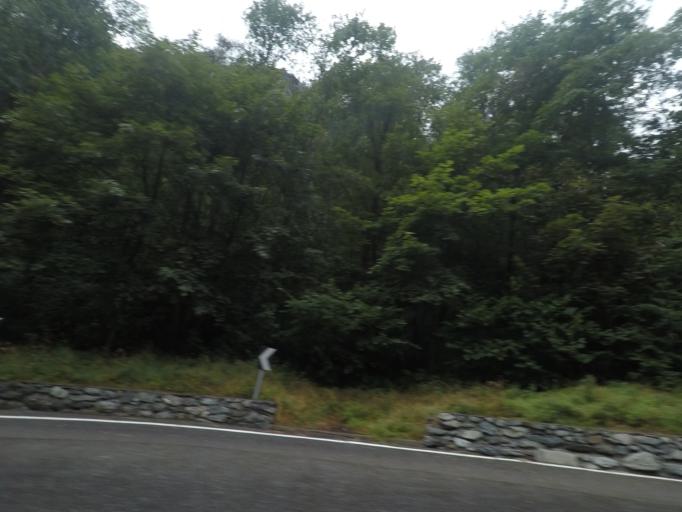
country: IT
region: Aosta Valley
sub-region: Valle d'Aosta
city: Chamois
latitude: 45.8479
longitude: 7.6044
